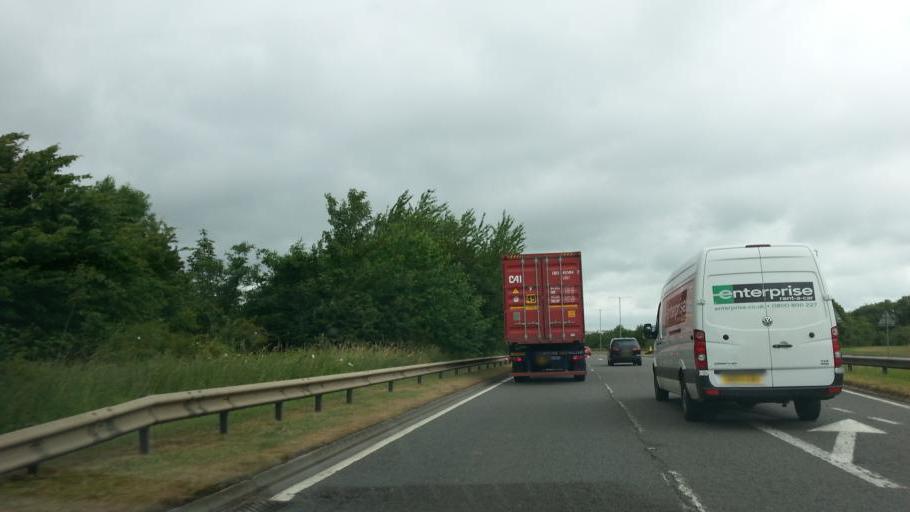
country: GB
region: England
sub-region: Northamptonshire
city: Corby
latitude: 52.4846
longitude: -0.6568
